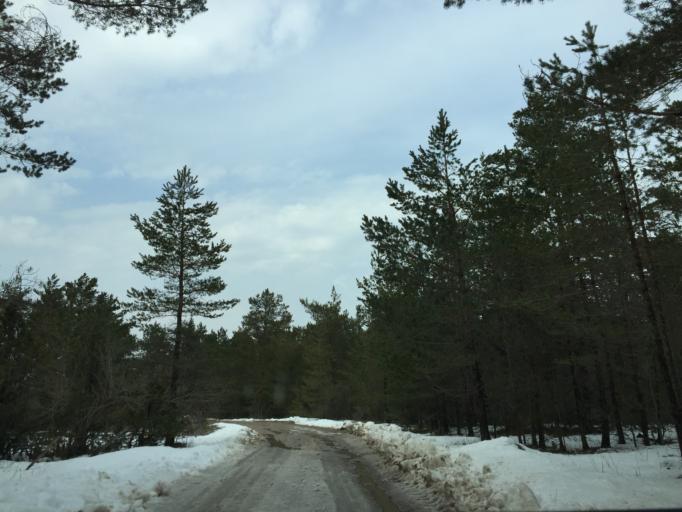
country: EE
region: Saare
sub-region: Kuressaare linn
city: Kuressaare
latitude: 58.4322
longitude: 22.1431
